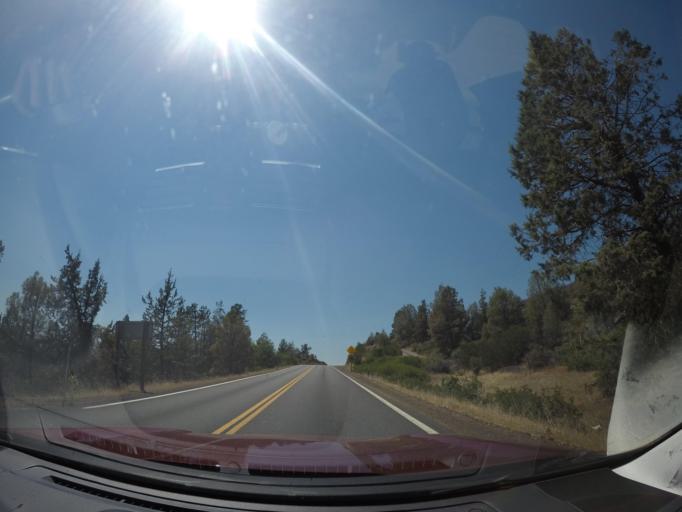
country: US
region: California
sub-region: Shasta County
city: Burney
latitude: 40.9924
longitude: -121.4751
